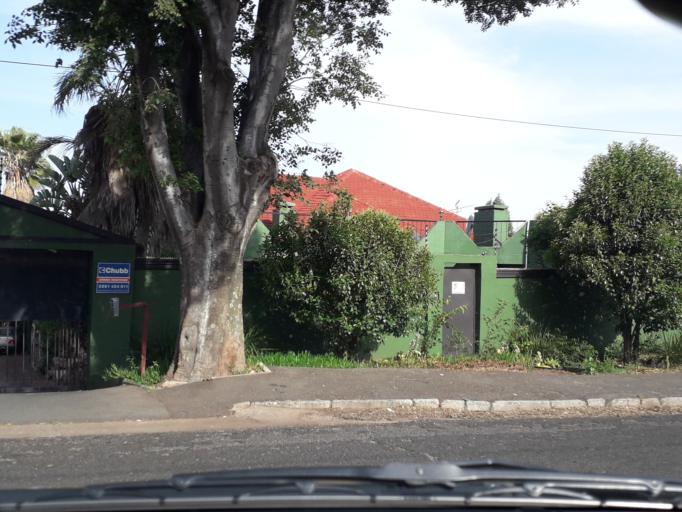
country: ZA
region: Gauteng
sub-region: City of Johannesburg Metropolitan Municipality
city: Johannesburg
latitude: -26.1736
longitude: 28.0976
